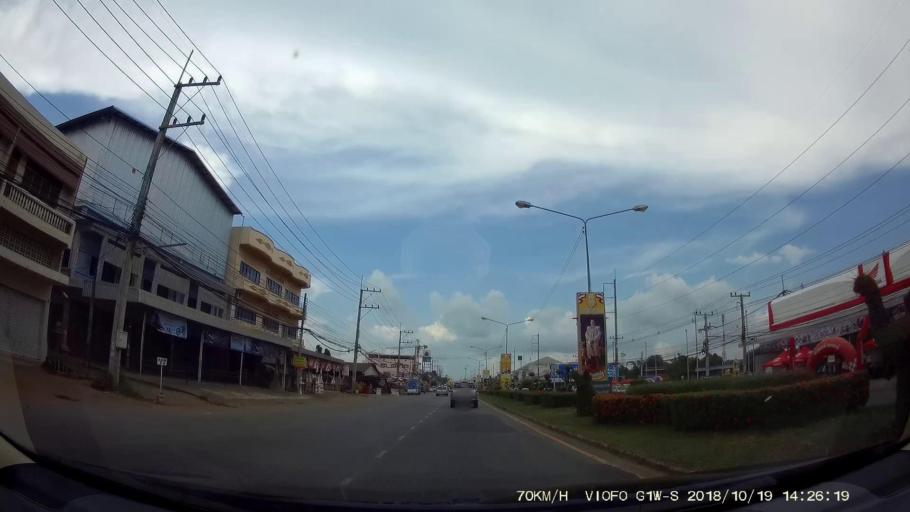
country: TH
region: Chaiyaphum
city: Kaeng Khro
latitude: 16.1051
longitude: 102.2602
